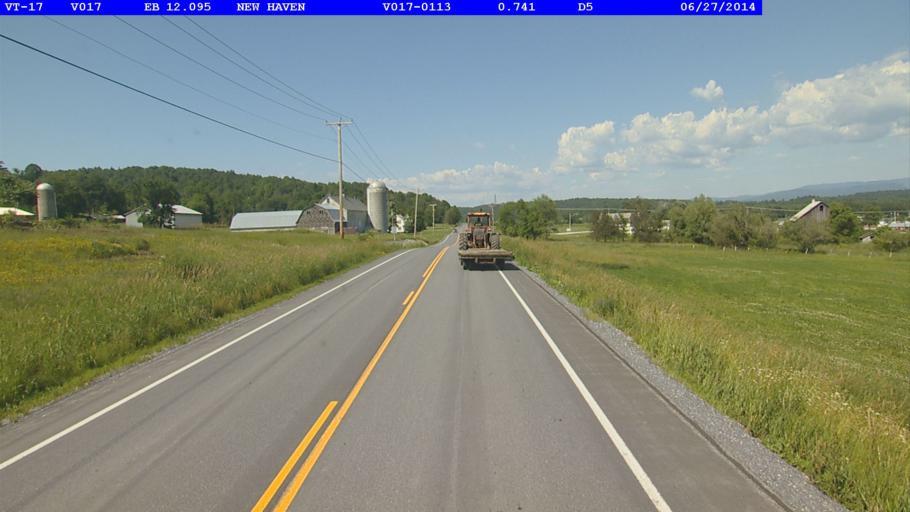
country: US
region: Vermont
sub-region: Addison County
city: Vergennes
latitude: 44.0907
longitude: -73.2342
